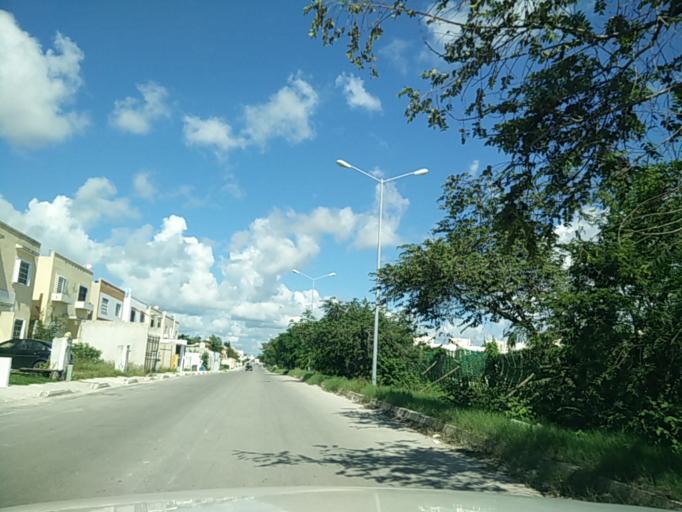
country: MX
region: Quintana Roo
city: Playa del Carmen
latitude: 20.6610
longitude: -87.0628
